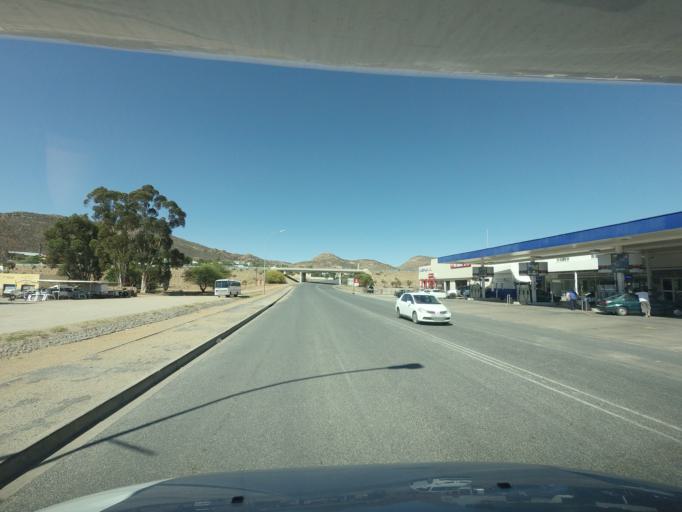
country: ZA
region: Northern Cape
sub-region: Namakwa District Municipality
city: Springbok
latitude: -29.6622
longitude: 17.8913
